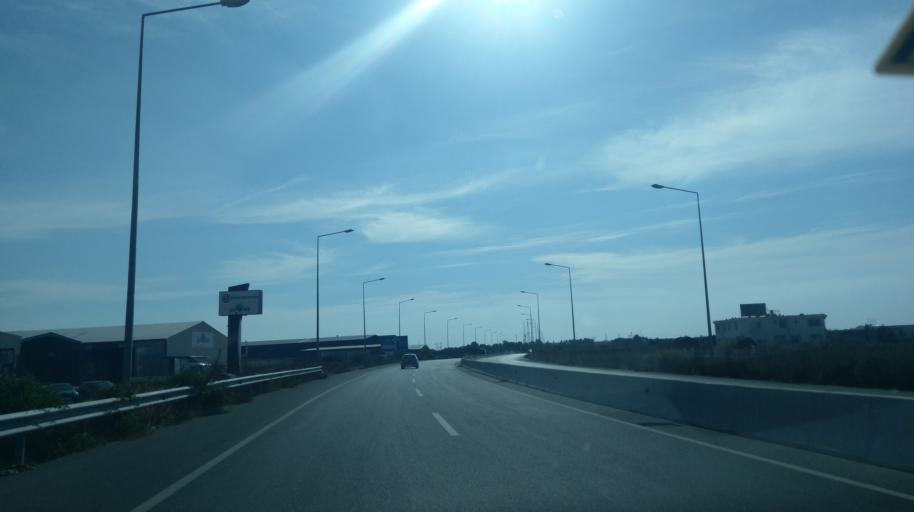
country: CY
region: Ammochostos
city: Famagusta
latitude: 35.1480
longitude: 33.8972
